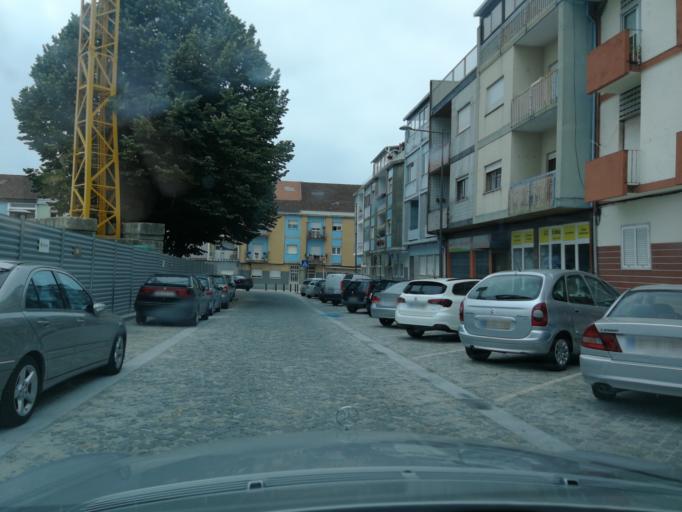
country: PT
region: Braga
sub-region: Braga
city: Braga
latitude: 41.5546
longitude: -8.4278
